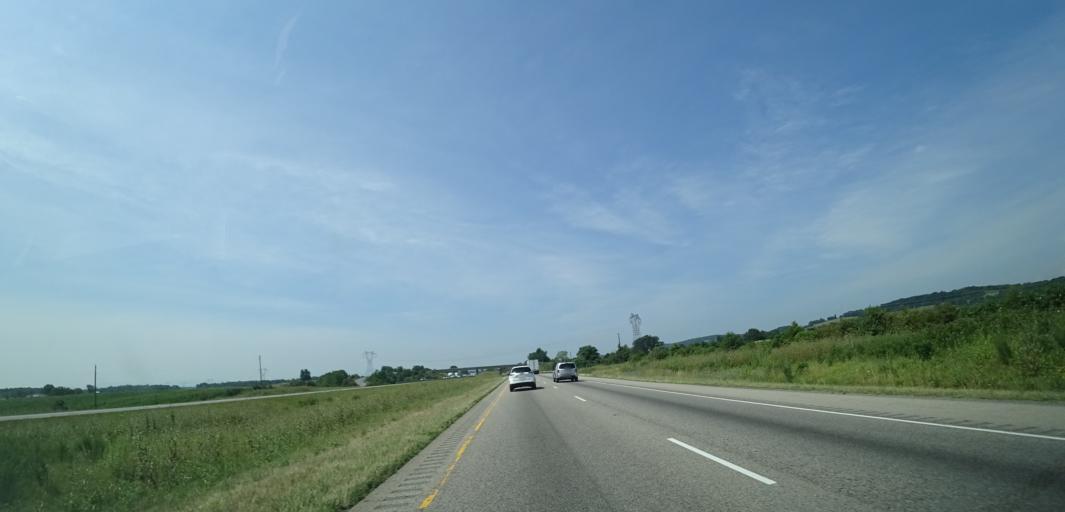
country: US
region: Virginia
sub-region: Augusta County
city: Weyers Cave
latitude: 38.2578
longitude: -78.9480
